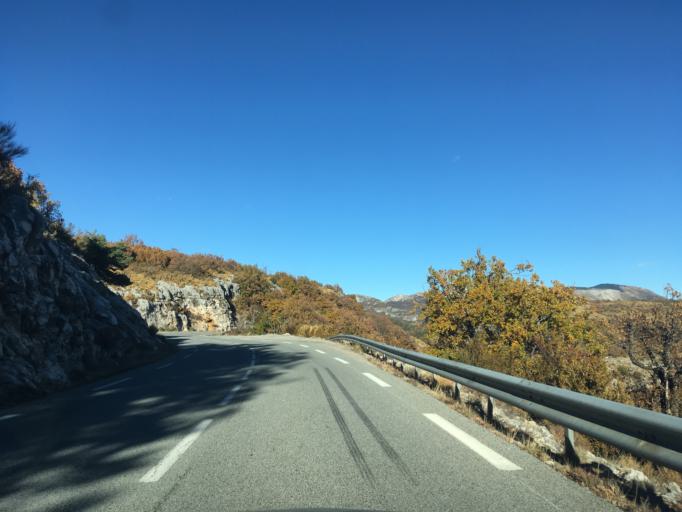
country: FR
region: Provence-Alpes-Cote d'Azur
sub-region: Departement du Var
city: Montferrat
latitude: 43.6988
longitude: 6.5051
